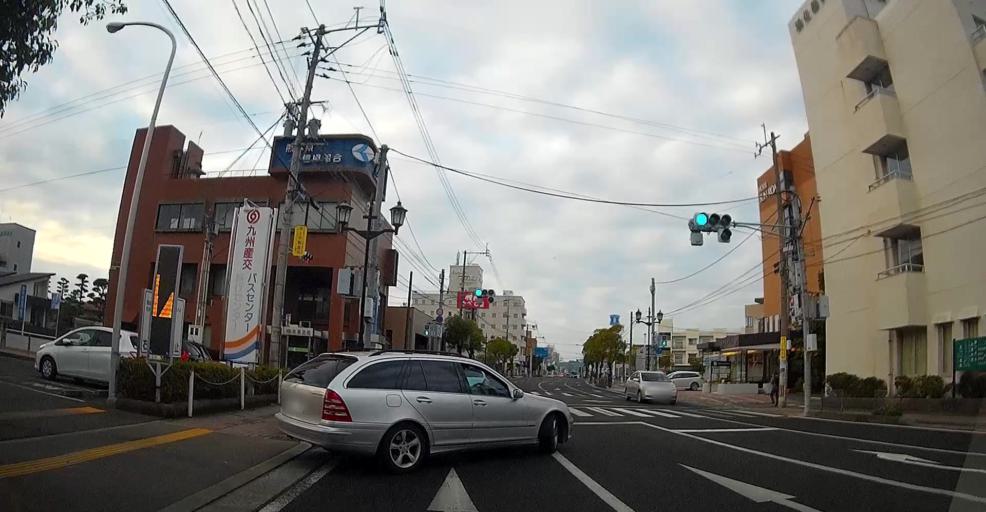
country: JP
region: Kumamoto
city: Hondo
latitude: 32.4540
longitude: 130.1945
